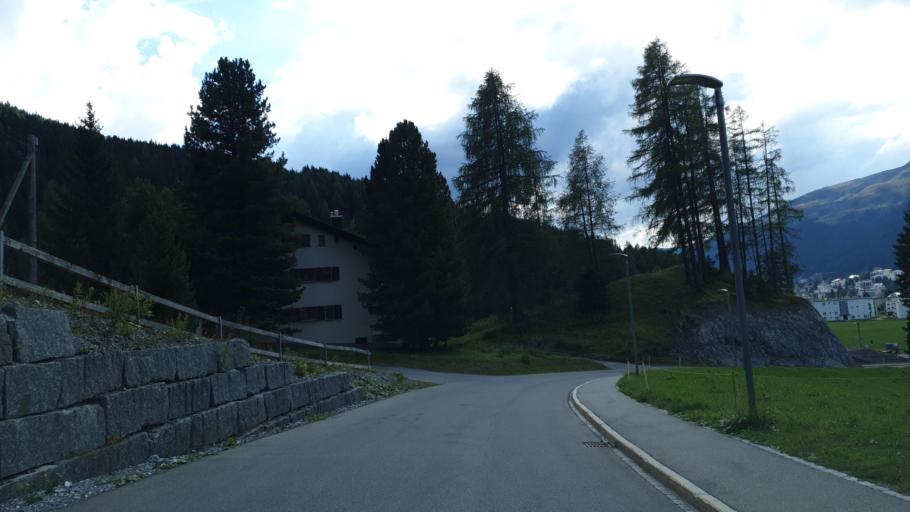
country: CH
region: Grisons
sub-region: Praettigau/Davos District
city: Davos
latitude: 46.8120
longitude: 9.8528
